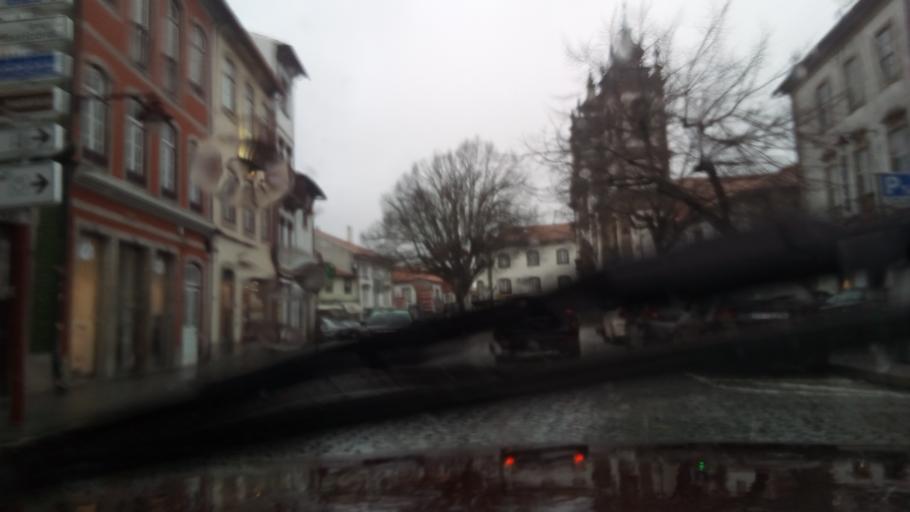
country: PT
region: Guarda
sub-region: Guarda
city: Guarda
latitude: 40.5379
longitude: -7.2678
